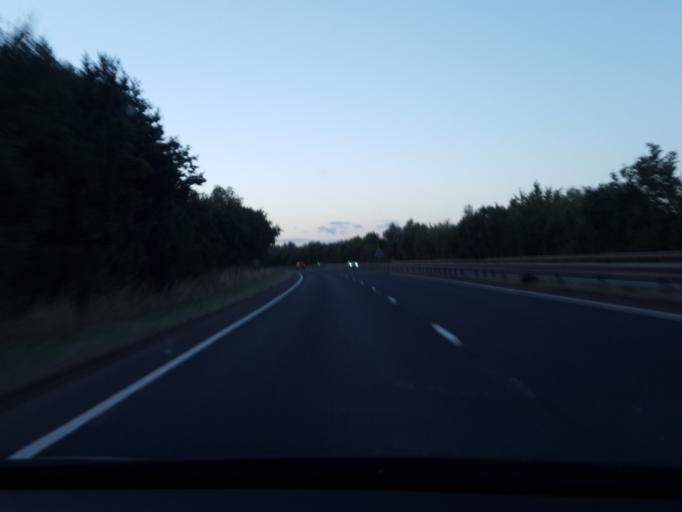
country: GB
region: England
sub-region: Leicestershire
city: Mountsorrel
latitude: 52.7082
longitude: -1.1242
